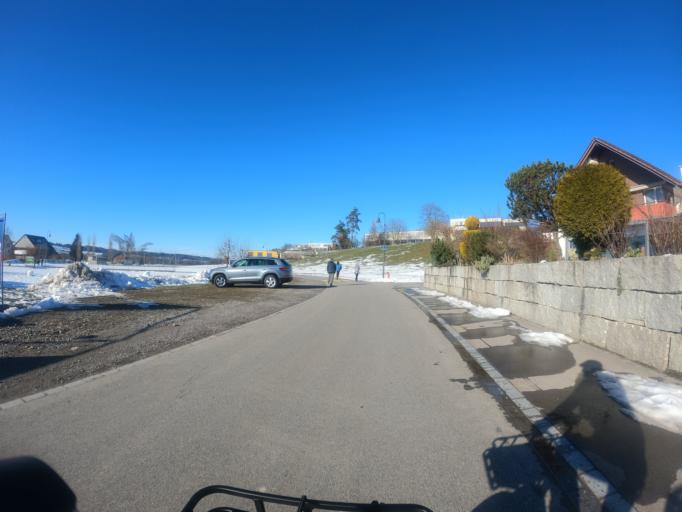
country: CH
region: Aargau
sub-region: Bezirk Bremgarten
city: Jonen
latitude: 47.2966
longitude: 8.3922
